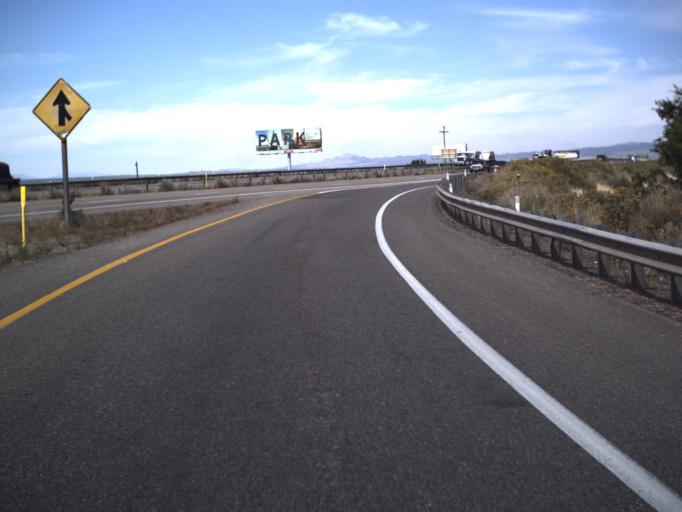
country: US
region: Utah
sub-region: Iron County
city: Cedar City
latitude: 37.6840
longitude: -113.0791
